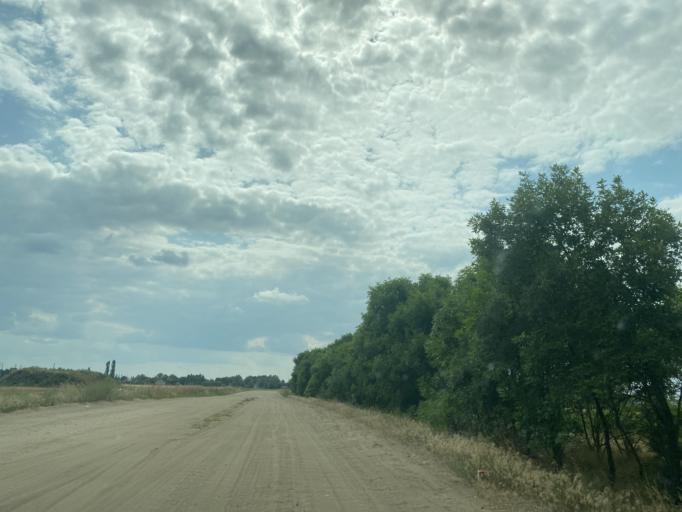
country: BY
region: Brest
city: Ivanava
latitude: 52.3585
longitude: 25.6329
